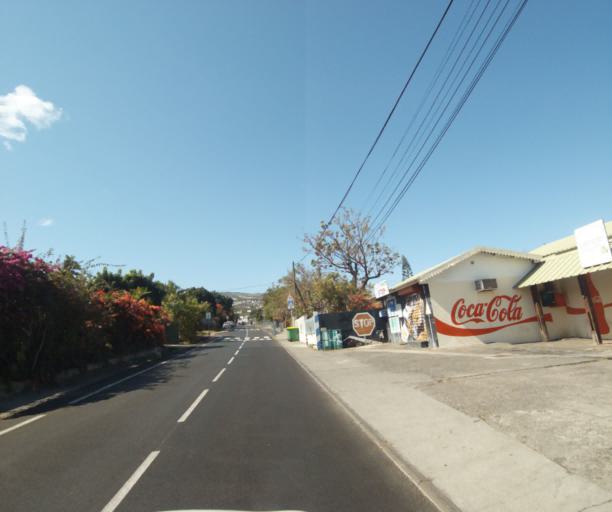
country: RE
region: Reunion
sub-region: Reunion
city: La Possession
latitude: -20.9790
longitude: 55.3240
